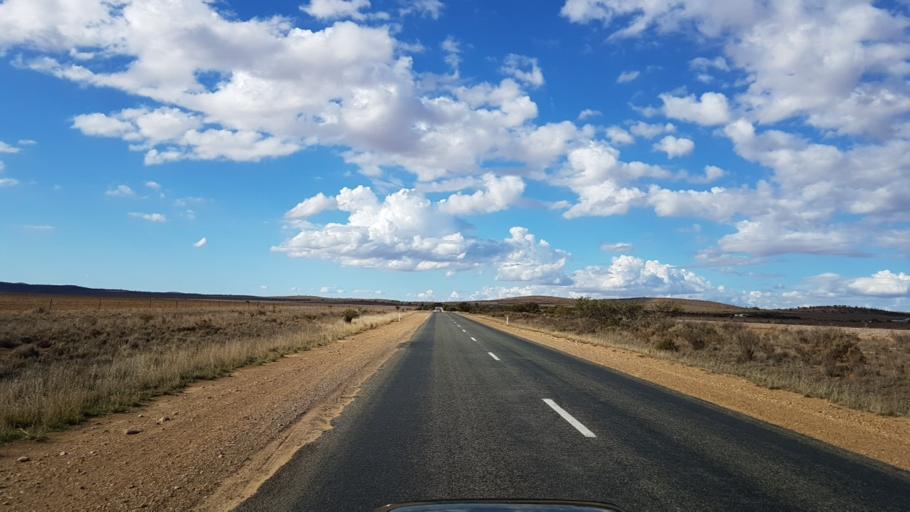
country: AU
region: South Australia
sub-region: Peterborough
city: Peterborough
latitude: -32.9661
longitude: 138.8757
